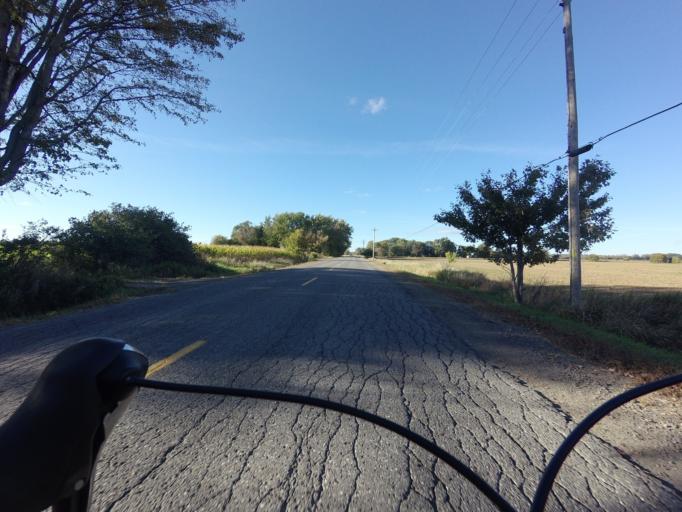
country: CA
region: Ontario
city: Bells Corners
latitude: 45.2125
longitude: -75.7973
